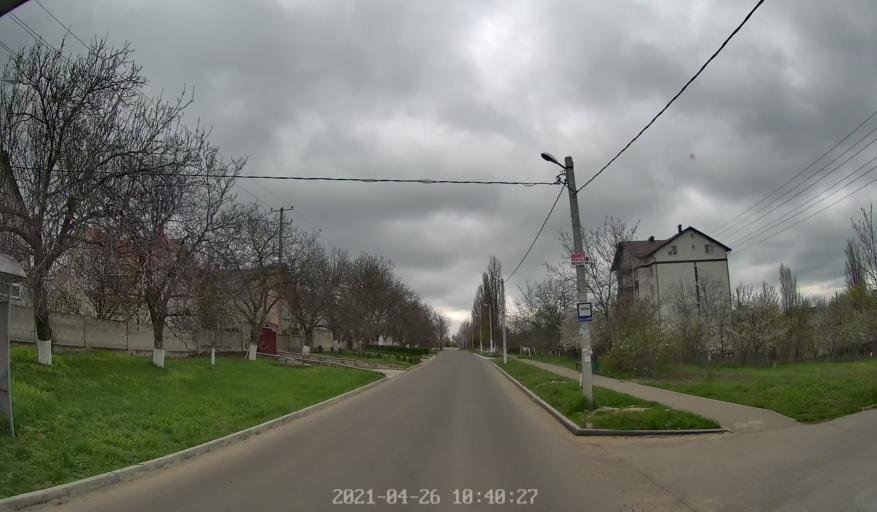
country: MD
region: Chisinau
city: Cricova
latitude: 47.1343
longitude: 28.8596
